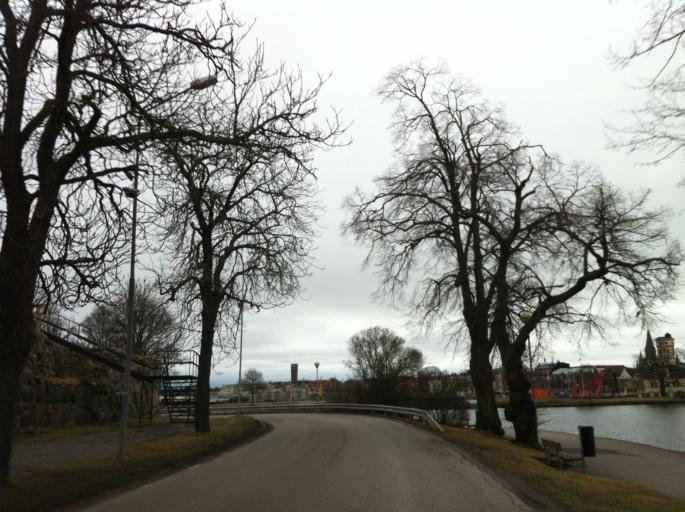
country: SE
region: Kalmar
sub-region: Vasterviks Kommun
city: Vaestervik
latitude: 57.8014
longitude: 16.6094
